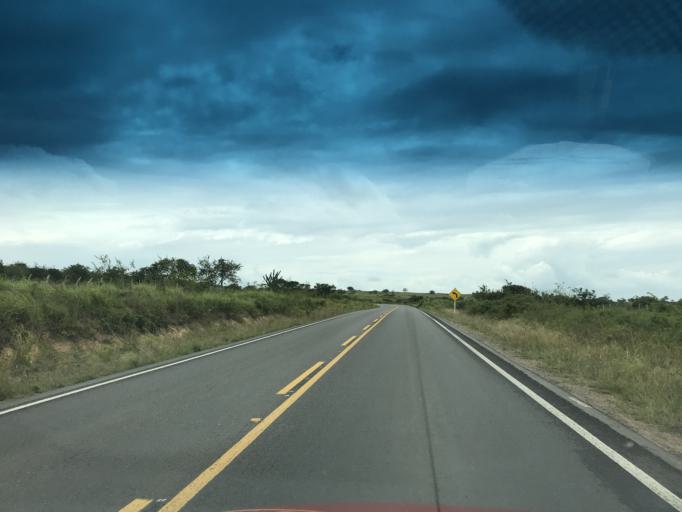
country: BR
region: Bahia
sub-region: Castro Alves
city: Castro Alves
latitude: -12.7541
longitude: -39.4092
